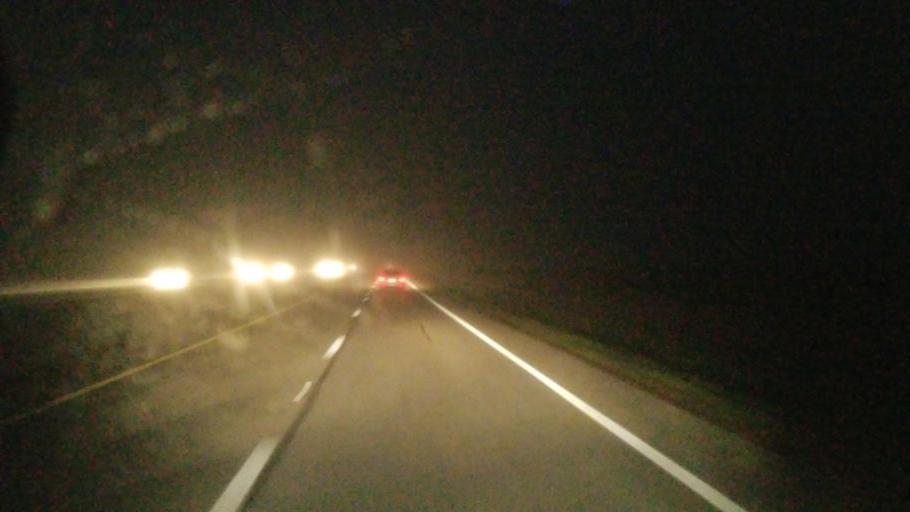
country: US
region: Ohio
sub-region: Pickaway County
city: Logan Elm Village
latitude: 39.5297
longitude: -82.9676
